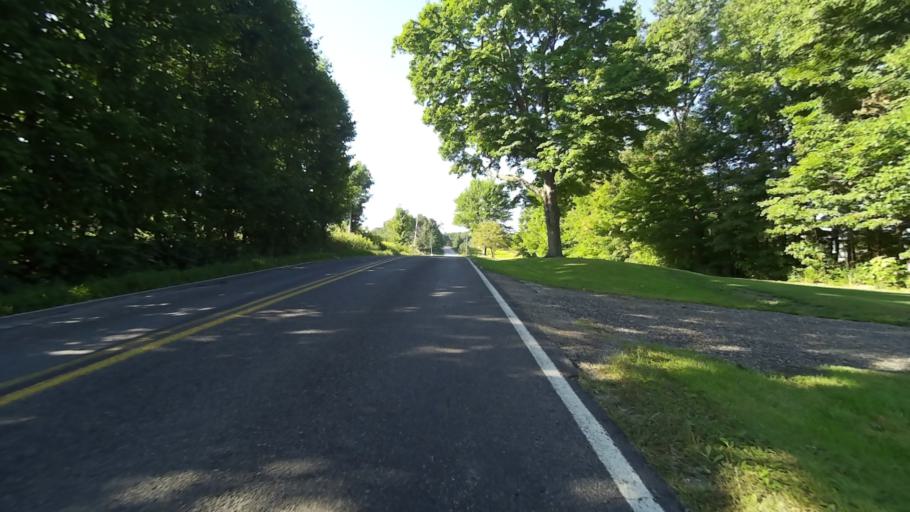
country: US
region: Ohio
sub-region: Portage County
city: Mantua
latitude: 41.2759
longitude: -81.2737
